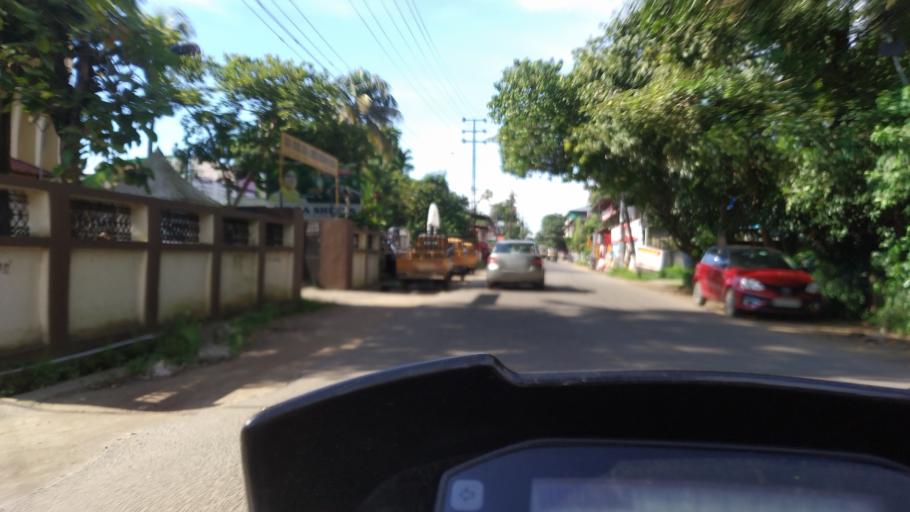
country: IN
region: Kerala
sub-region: Ernakulam
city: Elur
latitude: 10.0439
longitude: 76.2182
